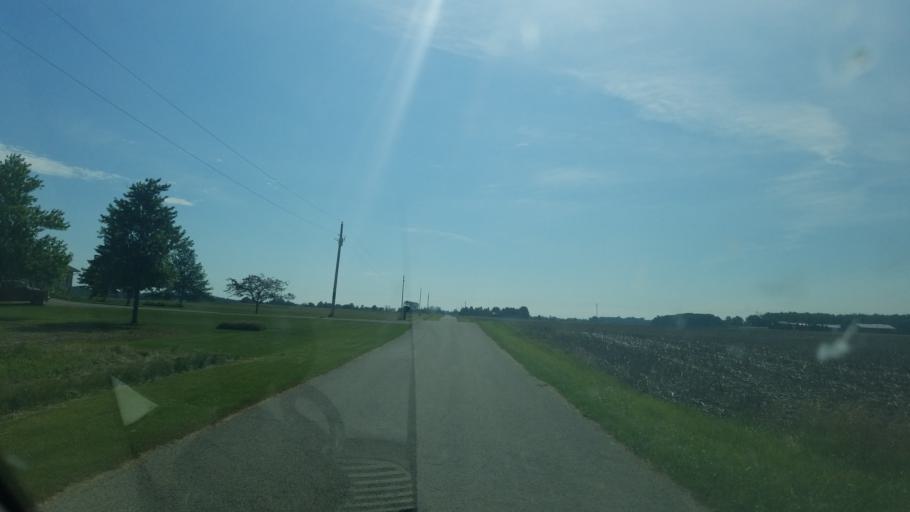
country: US
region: Ohio
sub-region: Wyandot County
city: Carey
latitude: 41.0142
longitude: -83.3438
